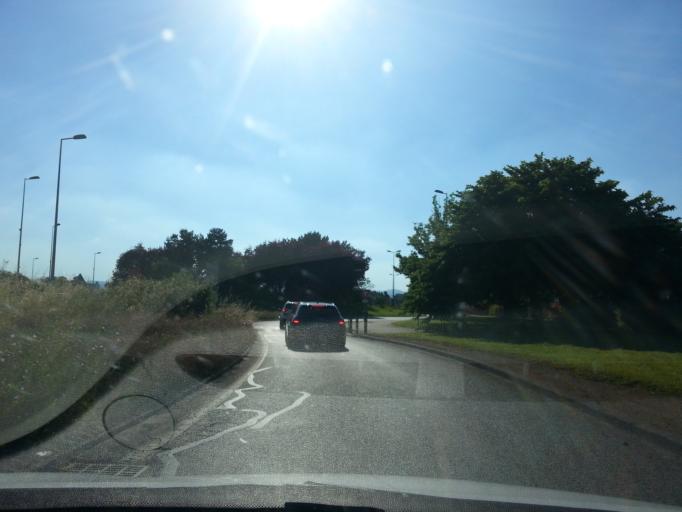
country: FR
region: Rhone-Alpes
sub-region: Departement du Rhone
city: Belleville
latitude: 46.1056
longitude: 4.7520
